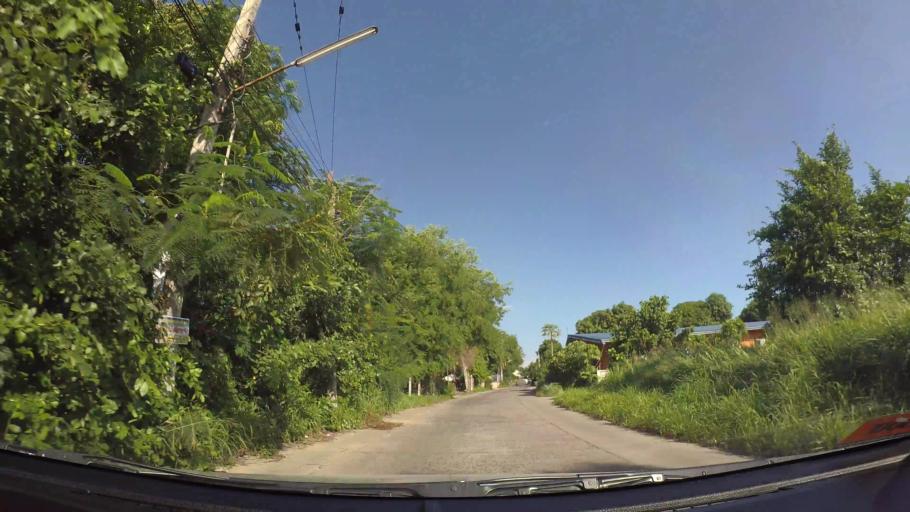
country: TH
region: Chon Buri
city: Si Racha
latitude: 13.1509
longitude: 100.9399
